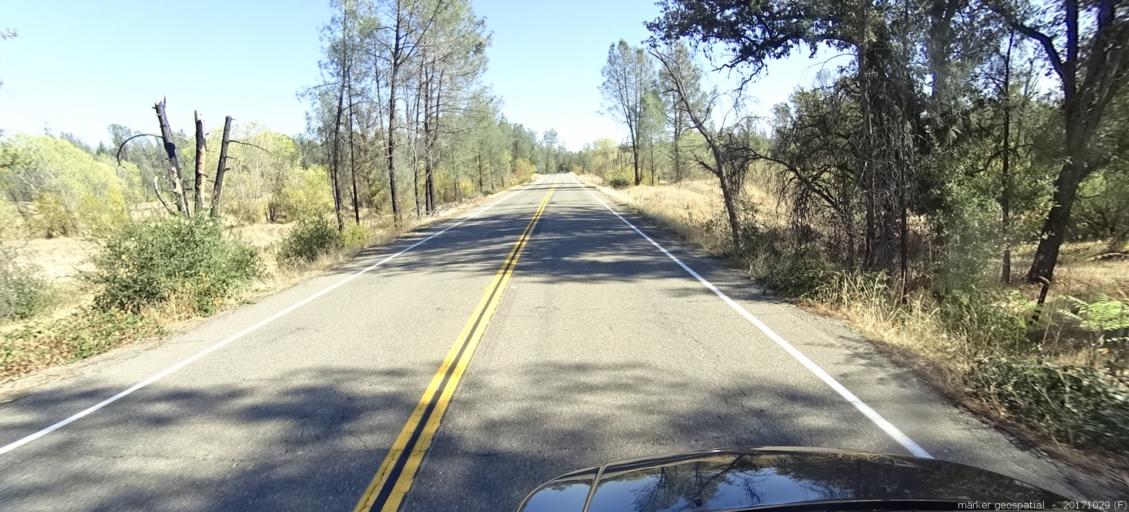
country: US
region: California
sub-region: Shasta County
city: Shasta
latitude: 40.4944
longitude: -122.4853
